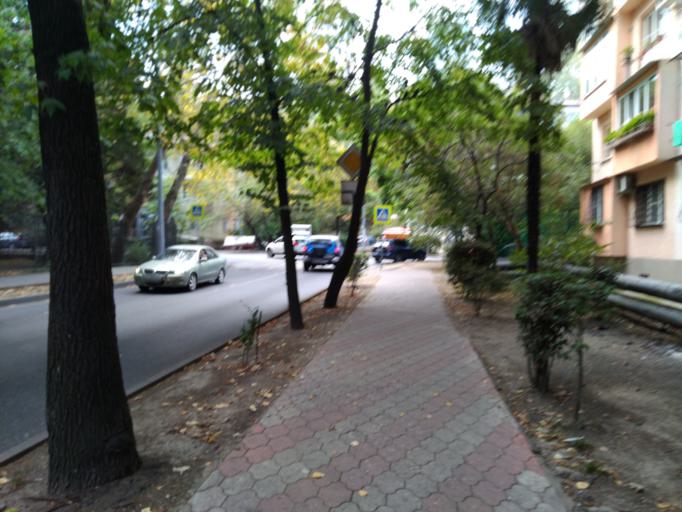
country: RU
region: Krasnodarskiy
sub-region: Sochi City
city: Sochi
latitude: 43.6026
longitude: 39.7228
